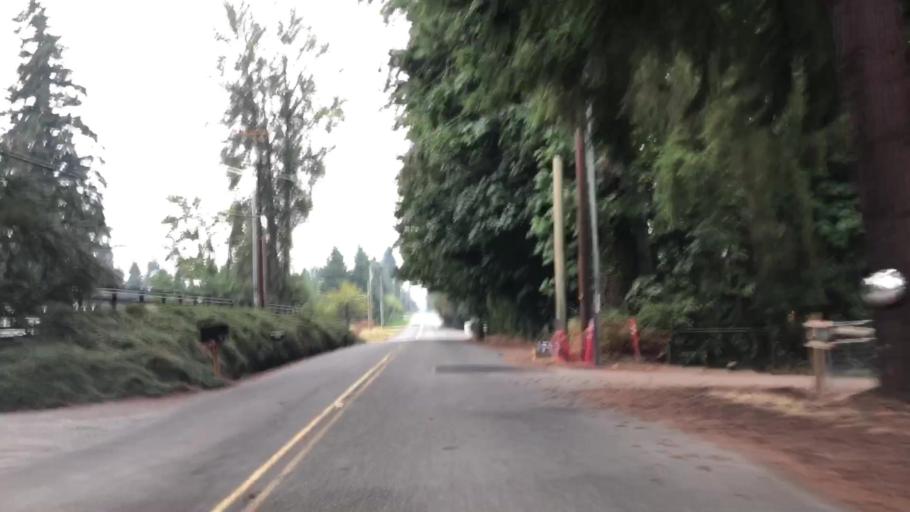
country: US
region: Washington
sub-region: King County
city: Cottage Lake
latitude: 47.7398
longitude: -122.1152
